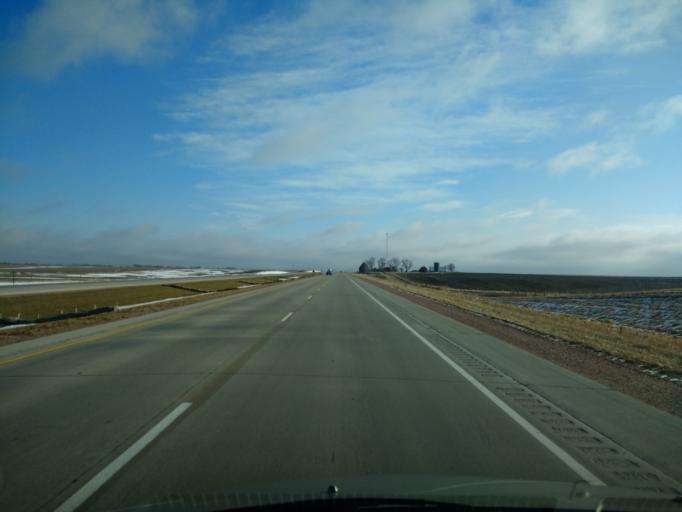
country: US
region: Iowa
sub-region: Ida County
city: Holstein
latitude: 42.4745
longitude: -95.5619
